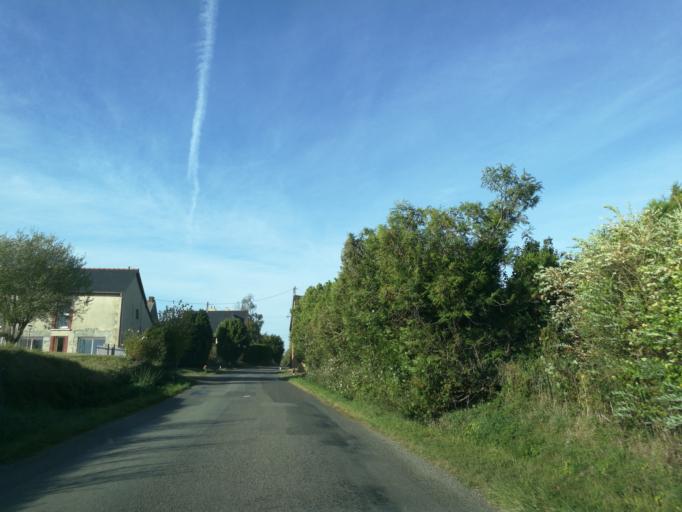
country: FR
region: Brittany
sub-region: Departement d'Ille-et-Vilaine
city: Montauban-de-Bretagne
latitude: 48.2019
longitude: -1.9925
